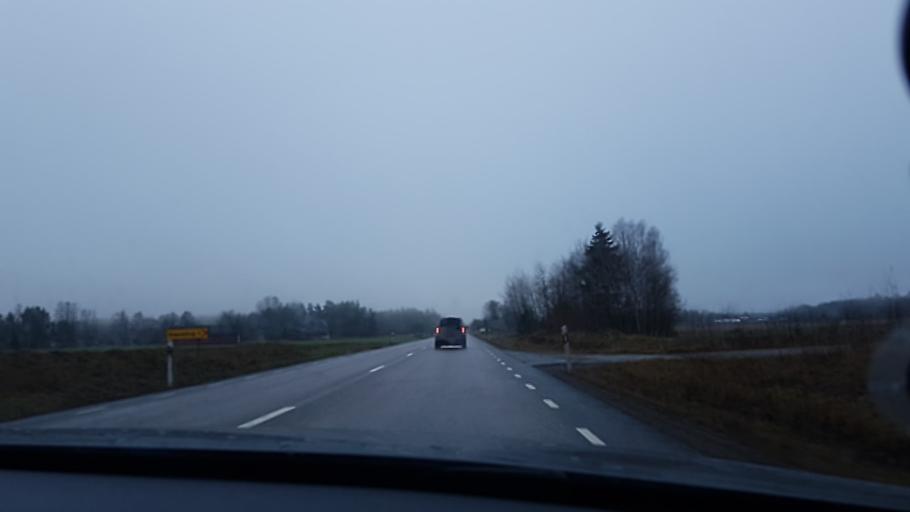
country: SE
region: Vaestra Goetaland
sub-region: Toreboda Kommun
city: Toereboda
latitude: 58.8104
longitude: 13.9786
